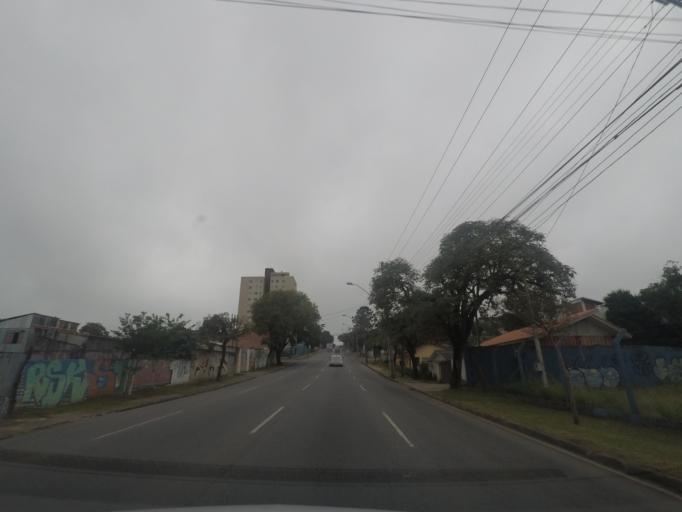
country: BR
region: Parana
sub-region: Curitiba
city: Curitiba
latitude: -25.3821
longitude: -49.2280
